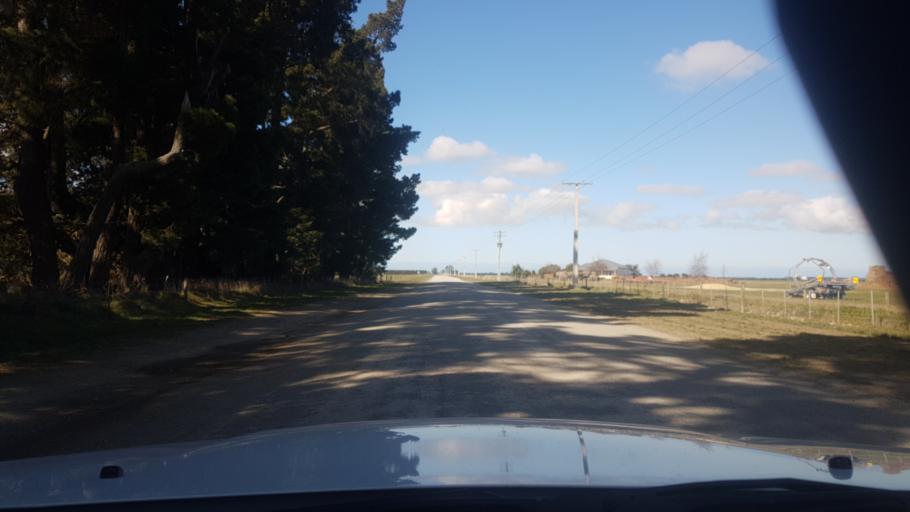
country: NZ
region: Canterbury
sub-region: Timaru District
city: Pleasant Point
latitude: -44.1189
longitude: 171.3930
